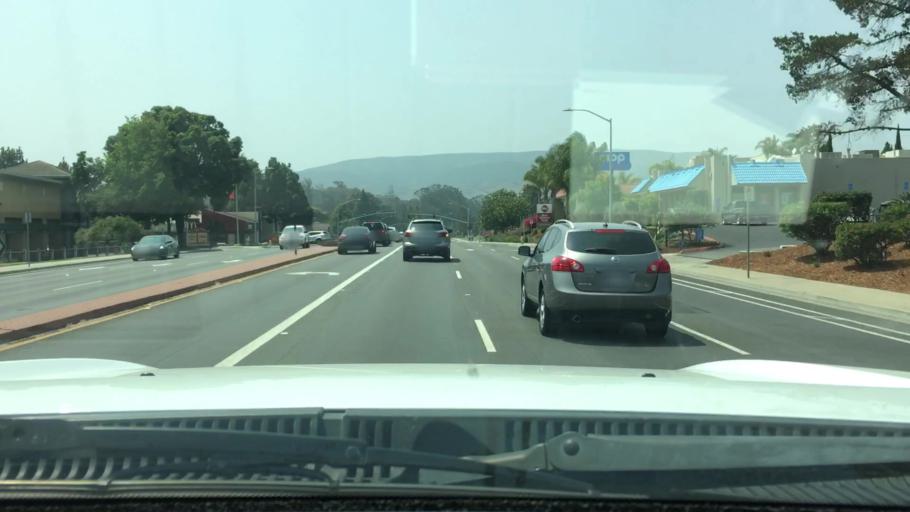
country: US
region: California
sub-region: San Luis Obispo County
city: San Luis Obispo
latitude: 35.2628
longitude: -120.6752
